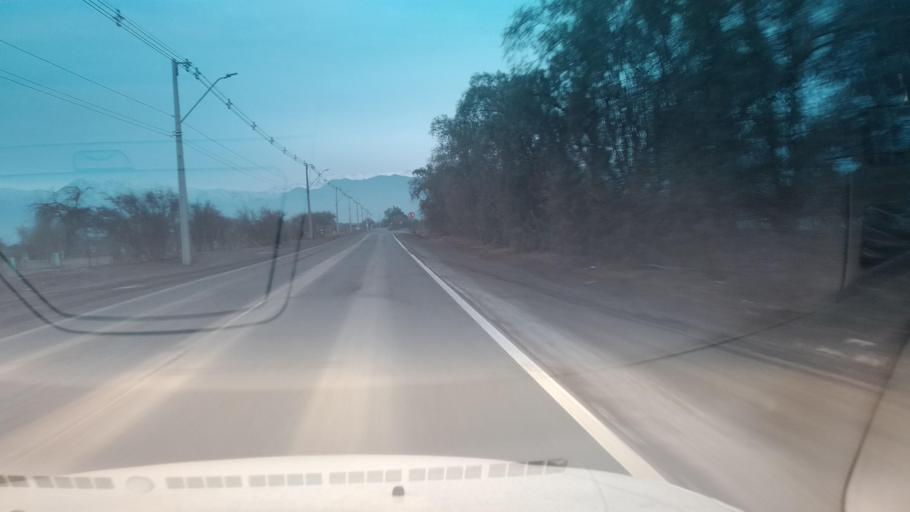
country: CL
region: Santiago Metropolitan
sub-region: Provincia de Chacabuco
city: Chicureo Abajo
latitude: -33.0936
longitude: -70.7439
